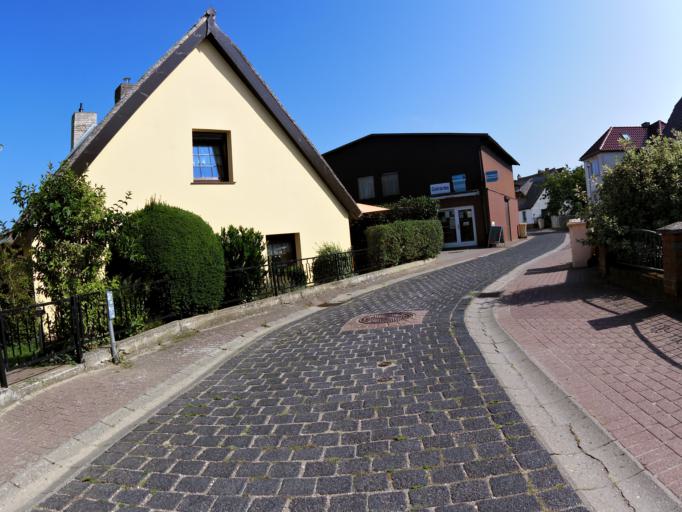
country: DE
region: Mecklenburg-Vorpommern
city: Loddin
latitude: 54.0120
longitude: 14.0460
